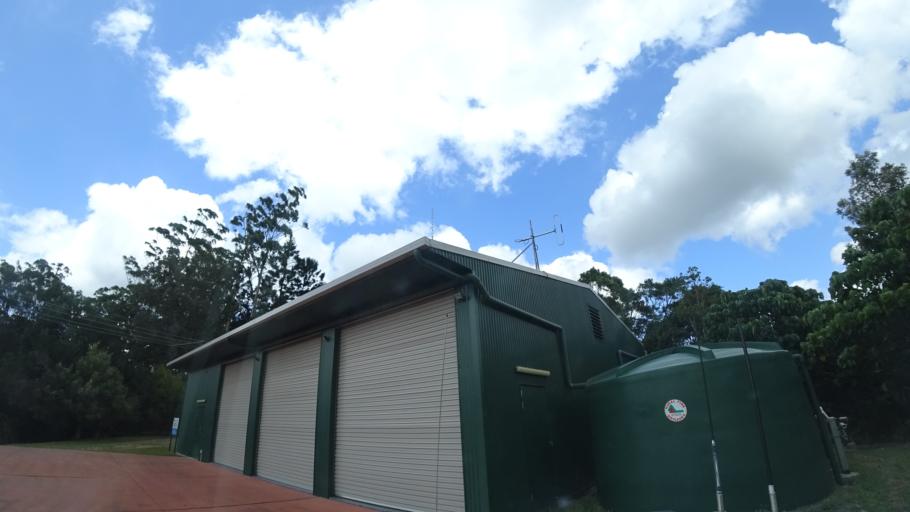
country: AU
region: Queensland
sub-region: Moreton Bay
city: Highvale
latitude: -27.3956
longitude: 152.7823
